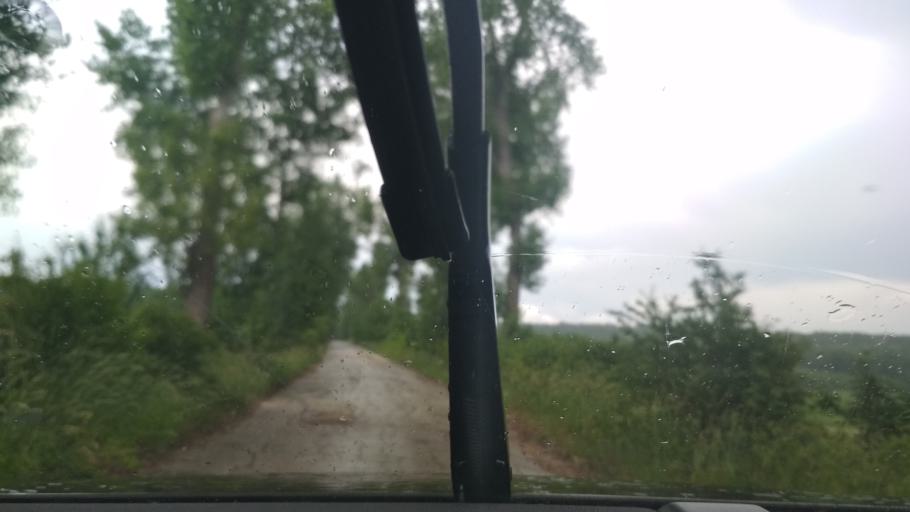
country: MD
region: Singerei
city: Biruinta
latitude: 47.7452
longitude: 28.1385
